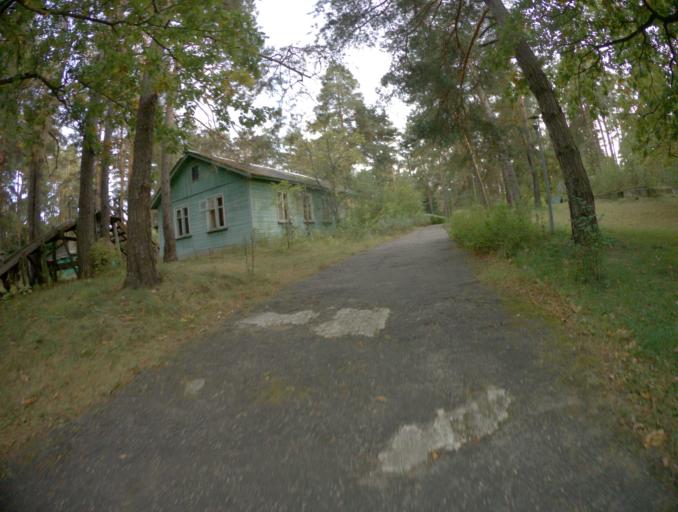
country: RU
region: Vladimir
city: Raduzhnyy
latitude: 56.0411
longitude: 40.3720
